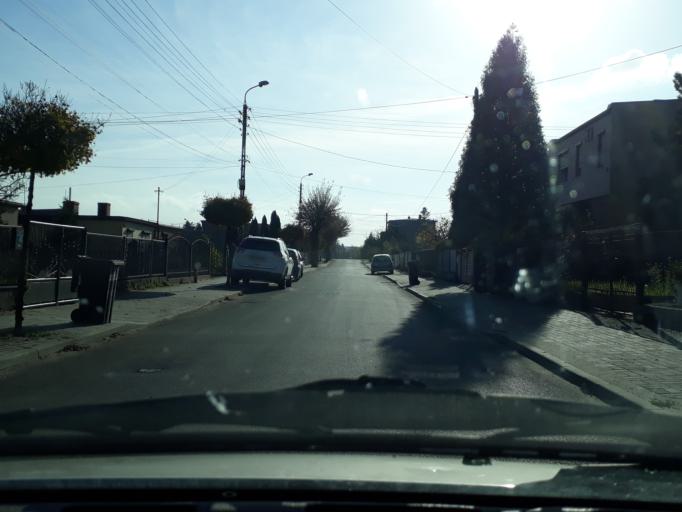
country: PL
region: Silesian Voivodeship
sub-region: Powiat tarnogorski
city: Tarnowskie Gory
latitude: 50.4330
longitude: 18.8442
